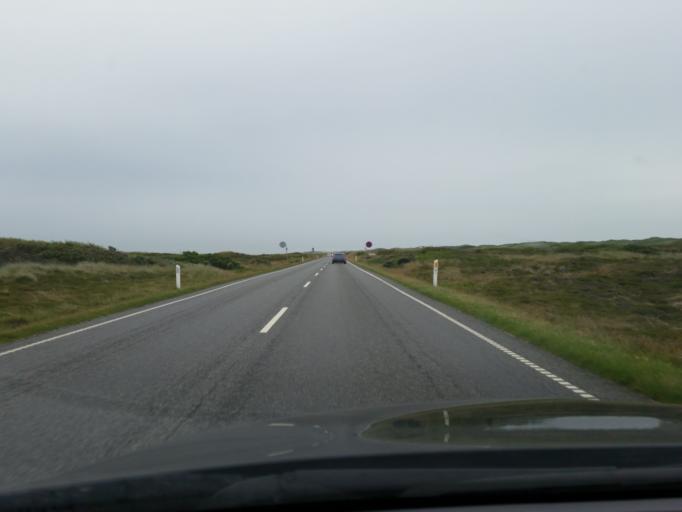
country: DK
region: Central Jutland
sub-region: Ringkobing-Skjern Kommune
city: Hvide Sande
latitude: 55.8383
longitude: 8.1728
